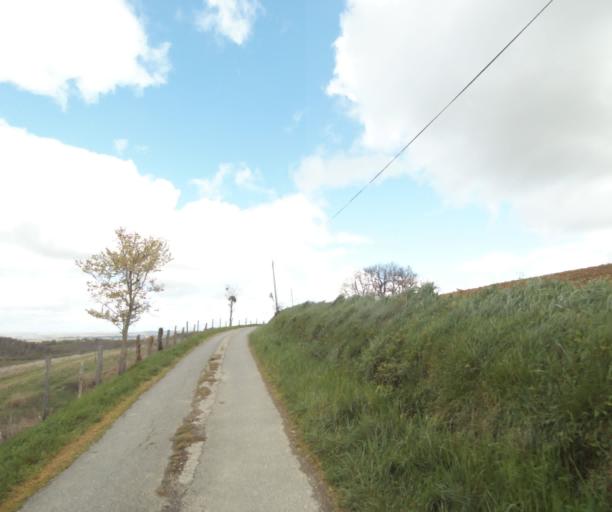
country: FR
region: Midi-Pyrenees
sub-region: Departement de l'Ariege
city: Saverdun
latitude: 43.2022
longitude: 1.5594
